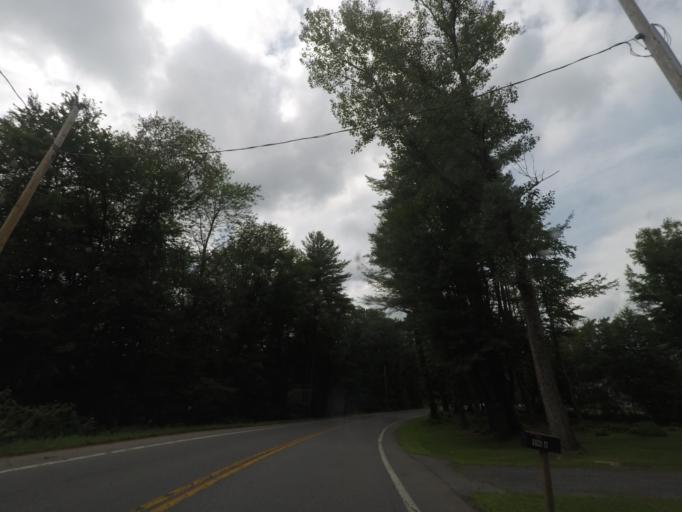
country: US
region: New York
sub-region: Saratoga County
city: Saratoga Springs
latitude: 43.0500
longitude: -73.6838
